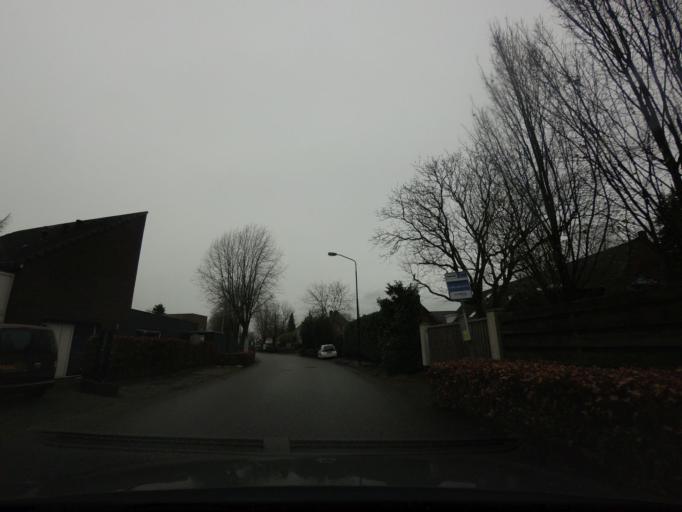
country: NL
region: North Brabant
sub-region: Gemeente Hilvarenbeek
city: Hilvarenbeek
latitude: 51.4849
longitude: 5.1475
